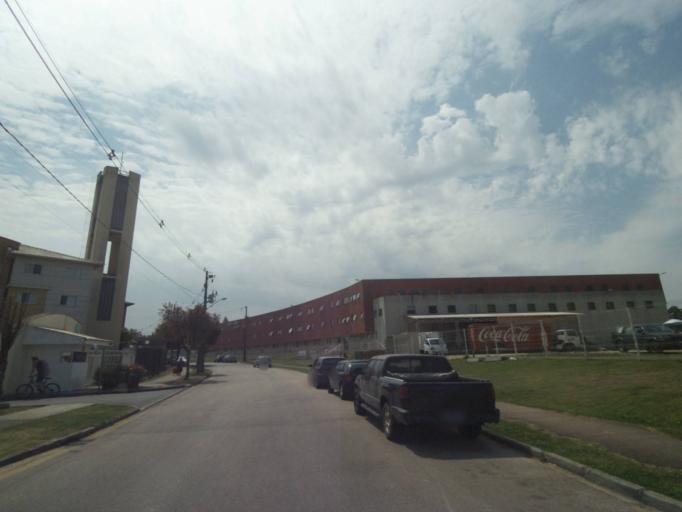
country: BR
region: Parana
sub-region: Curitiba
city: Curitiba
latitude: -25.4763
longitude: -49.3279
